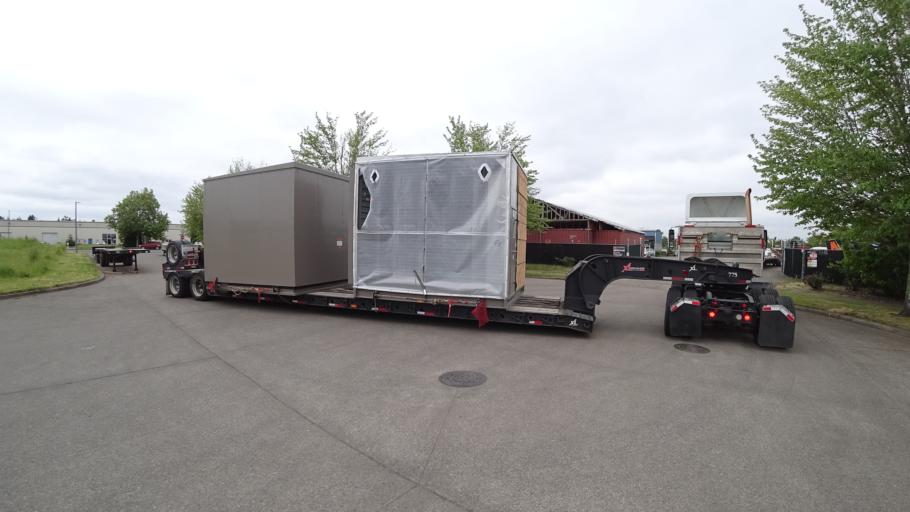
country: US
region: Oregon
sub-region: Washington County
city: Aloha
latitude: 45.4987
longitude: -122.9230
